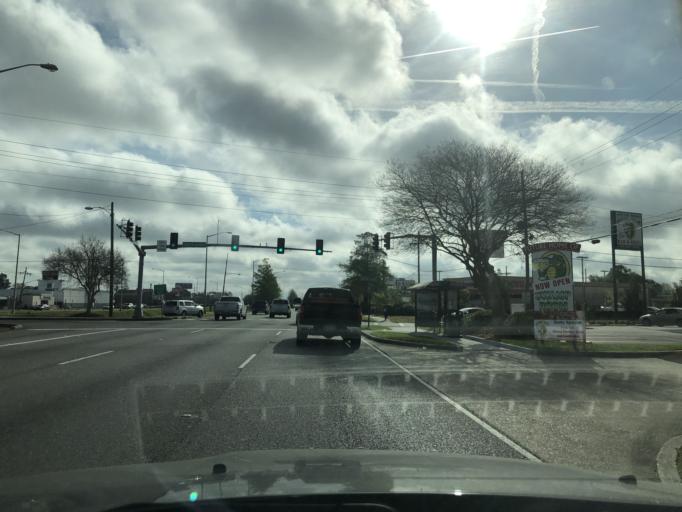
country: US
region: Louisiana
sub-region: Jefferson Parish
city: Kenner
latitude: 30.0059
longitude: -90.2015
